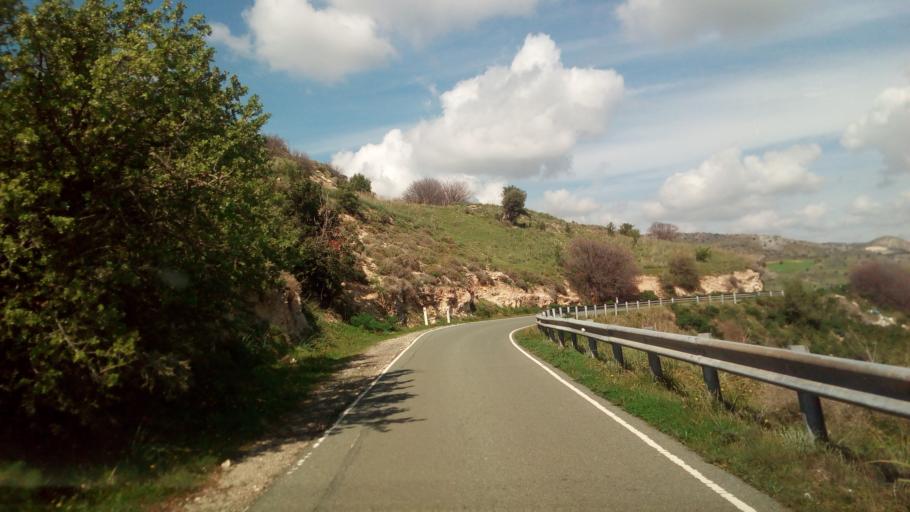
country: CY
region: Pafos
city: Mesogi
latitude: 34.7554
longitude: 32.5544
